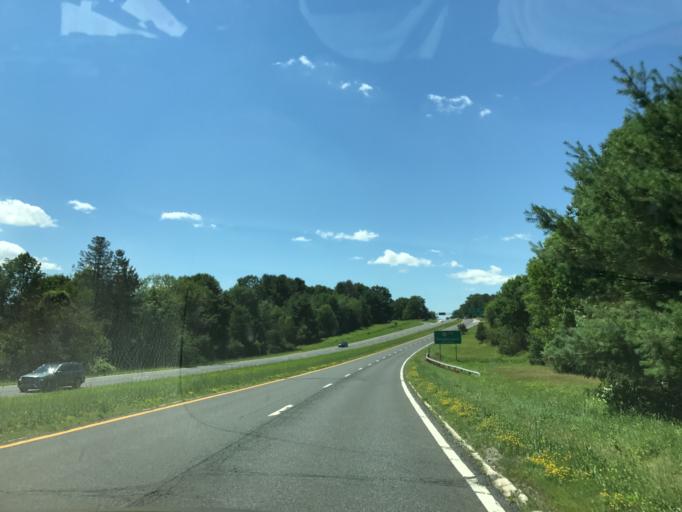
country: US
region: New York
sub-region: Dutchess County
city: Hillside Lake
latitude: 41.6757
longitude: -73.7874
